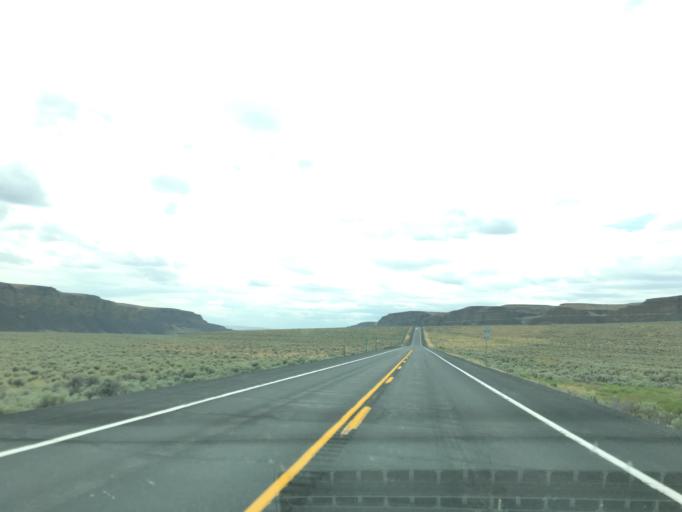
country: US
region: Washington
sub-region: Grant County
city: Soap Lake
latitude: 47.5977
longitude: -119.6723
